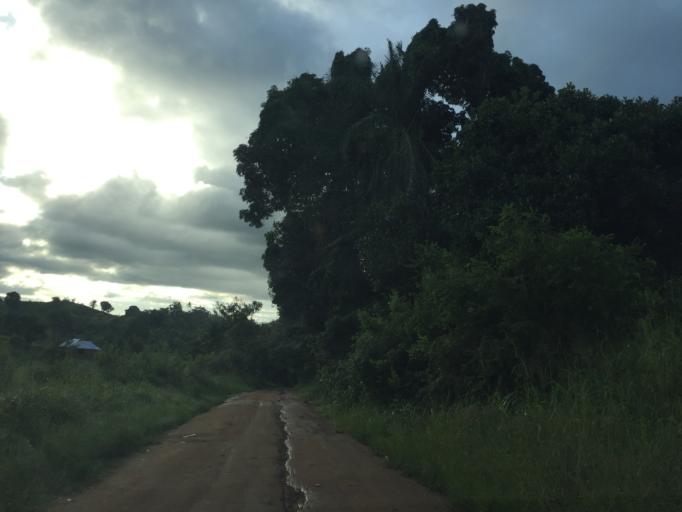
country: TZ
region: Tanga
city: Muheza
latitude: -5.1633
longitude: 38.7715
